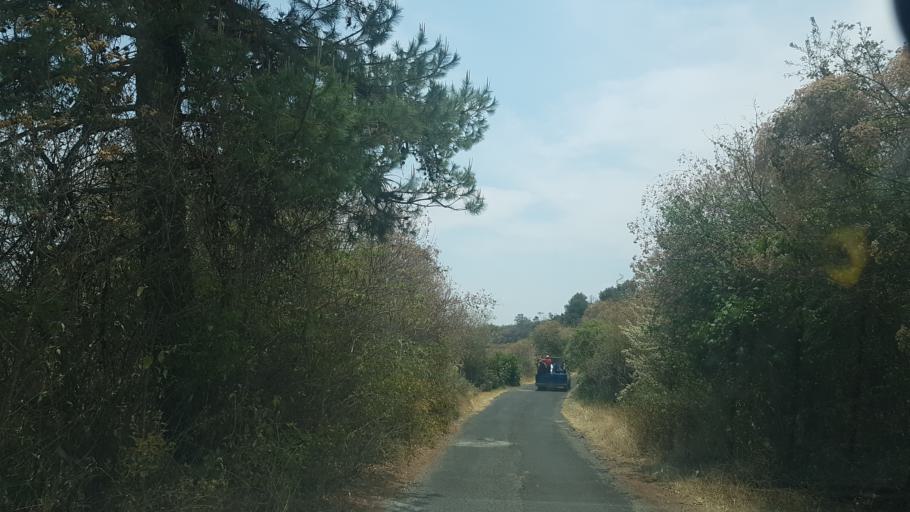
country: MX
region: Puebla
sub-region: Atzitzihuacan
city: Santiago Atzitzihuacan
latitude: 18.8500
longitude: -98.6106
